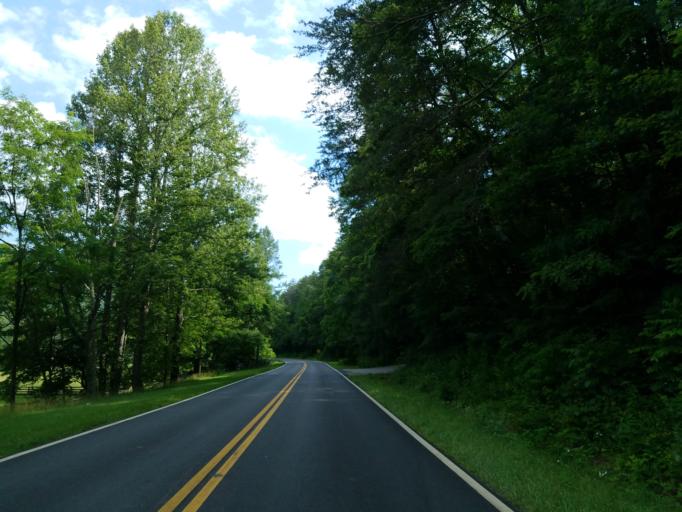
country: US
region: Georgia
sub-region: Fannin County
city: Blue Ridge
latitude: 34.8370
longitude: -84.2981
